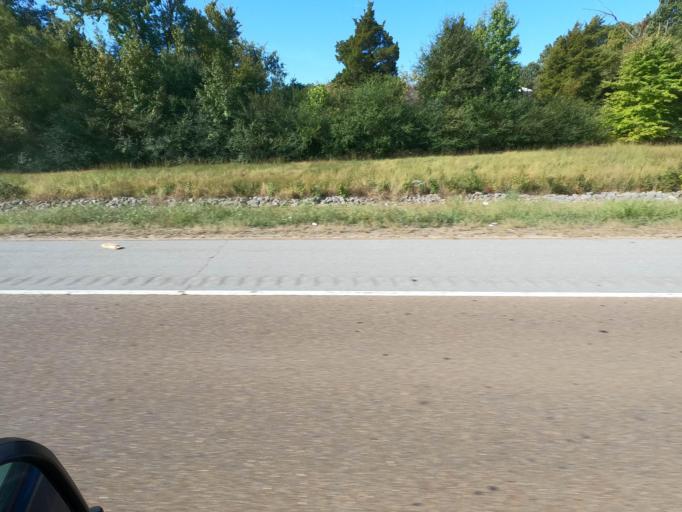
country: US
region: Tennessee
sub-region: Shelby County
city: Arlington
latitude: 35.2763
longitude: -89.6795
